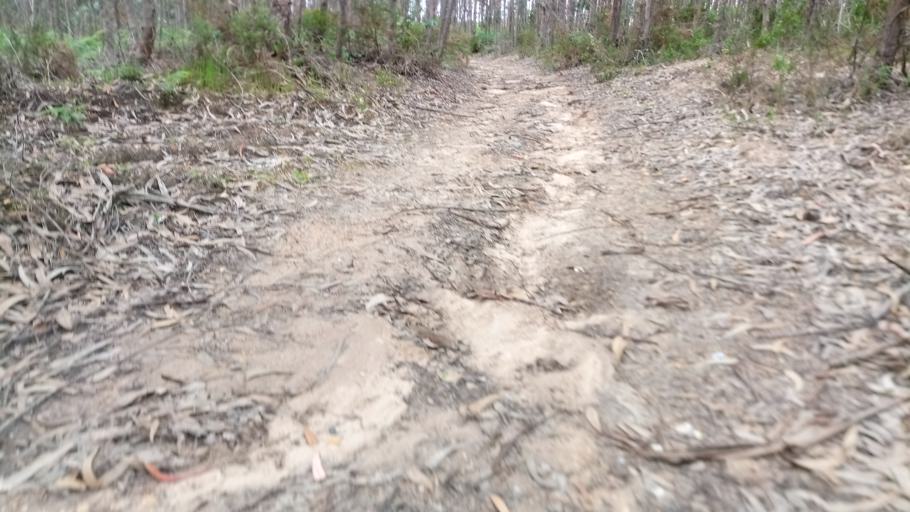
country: PT
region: Leiria
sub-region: Obidos
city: Obidos
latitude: 39.3920
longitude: -9.2089
